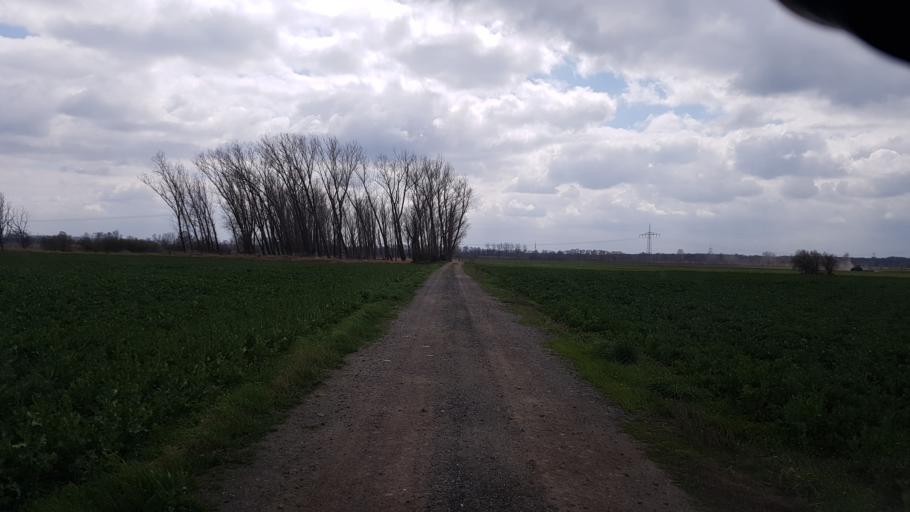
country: DE
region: Brandenburg
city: Schraden
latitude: 51.4681
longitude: 13.6810
